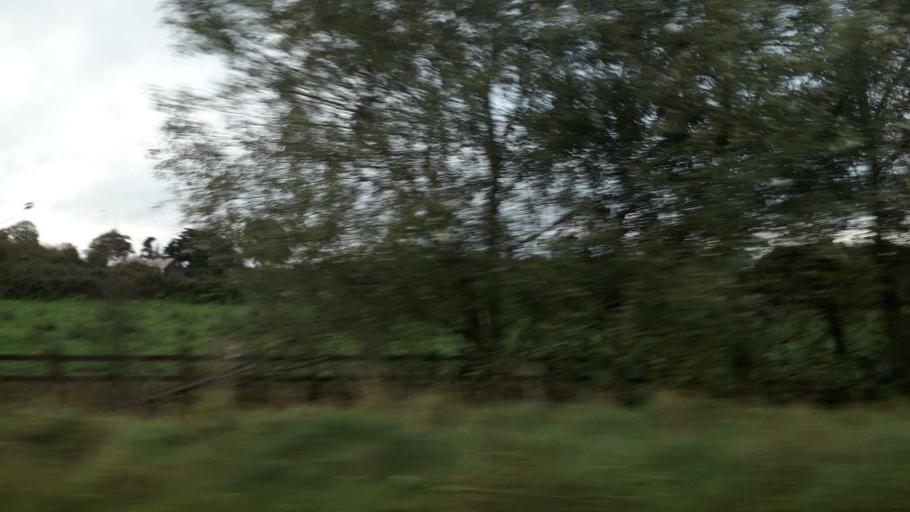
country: IE
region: Leinster
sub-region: An Longfort
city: Lanesborough
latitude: 53.7616
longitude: -8.0002
